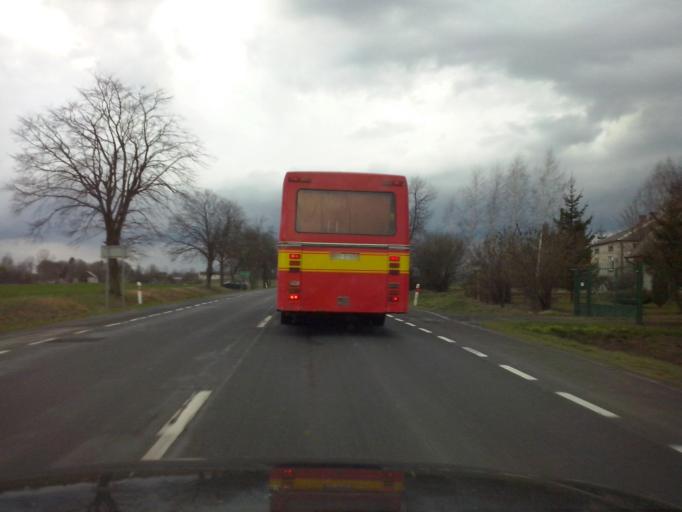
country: PL
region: Lublin Voivodeship
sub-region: Powiat chelmski
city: Rejowiec Fabryczny
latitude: 51.1730
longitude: 23.2825
